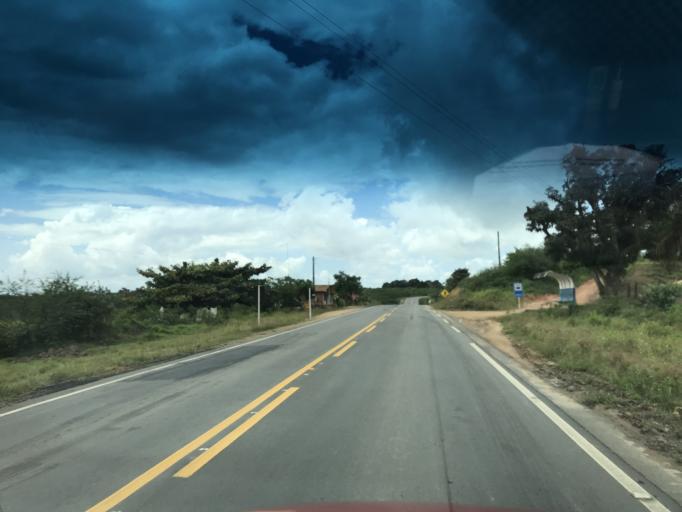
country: BR
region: Bahia
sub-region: Conceicao Do Almeida
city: Conceicao do Almeida
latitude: -12.6995
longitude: -39.2397
